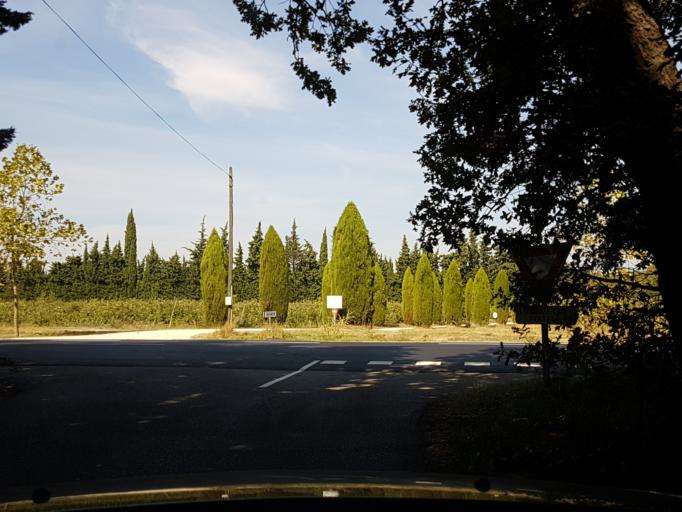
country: FR
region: Provence-Alpes-Cote d'Azur
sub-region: Departement des Bouches-du-Rhone
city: Molleges
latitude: 43.7850
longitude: 4.9218
